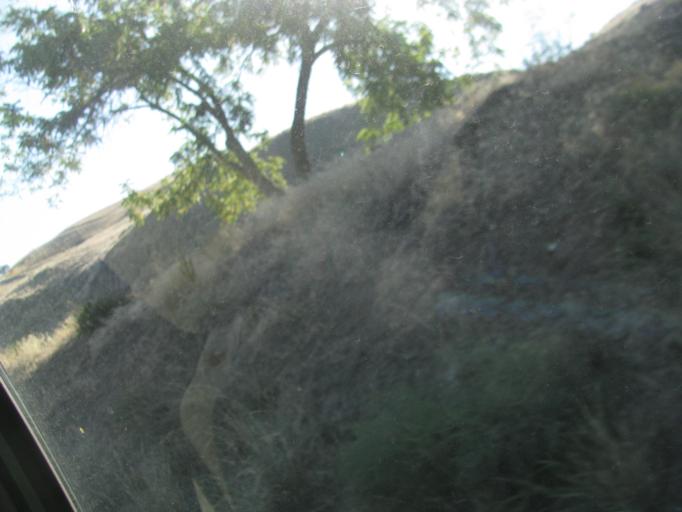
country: US
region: Washington
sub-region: Asotin County
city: Asotin
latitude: 46.3463
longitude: -117.0612
